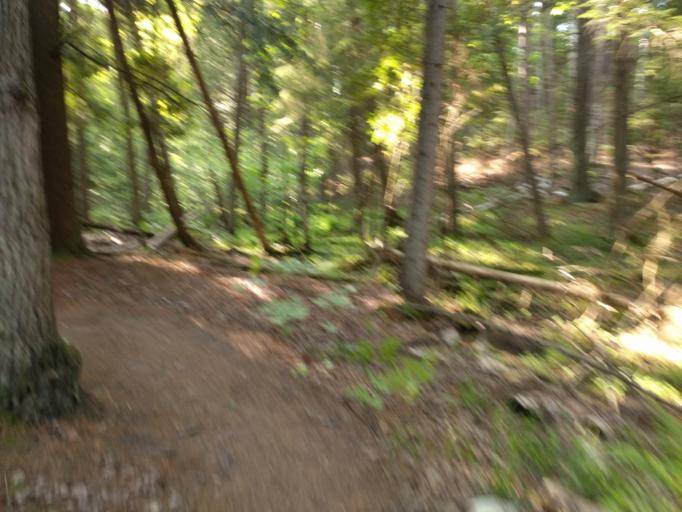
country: US
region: Michigan
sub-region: Marquette County
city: Trowbridge Park
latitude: 46.5687
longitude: -87.4511
